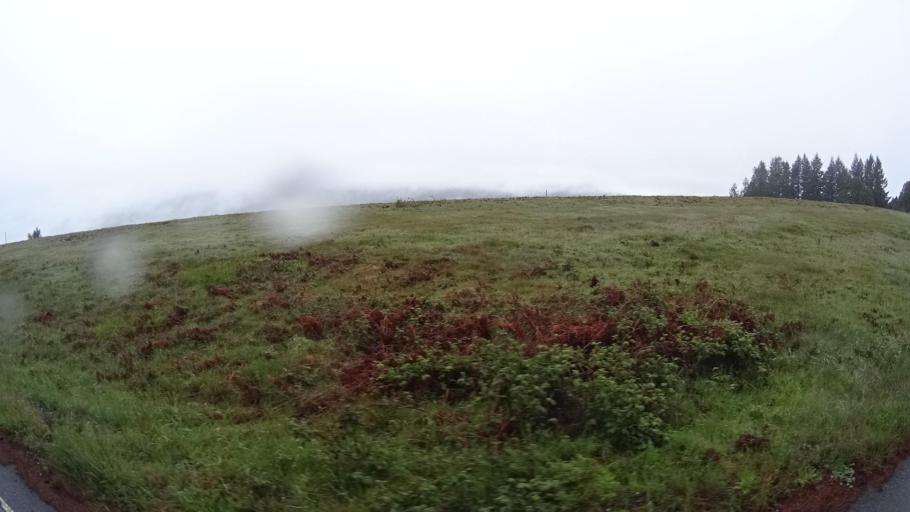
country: US
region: California
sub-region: Humboldt County
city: Westhaven-Moonstone
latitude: 41.1951
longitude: -123.9403
